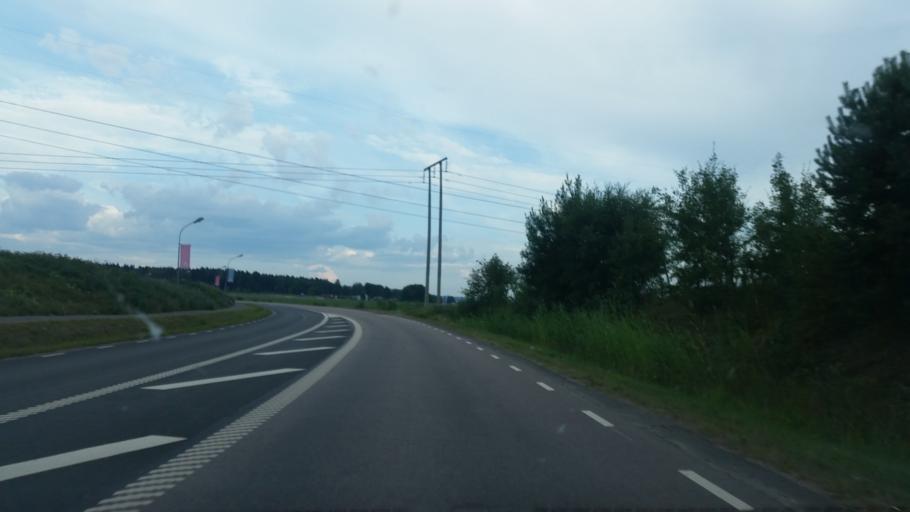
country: SE
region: Vaestra Goetaland
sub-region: Skara Kommun
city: Axvall
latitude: 58.4011
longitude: 13.5520
